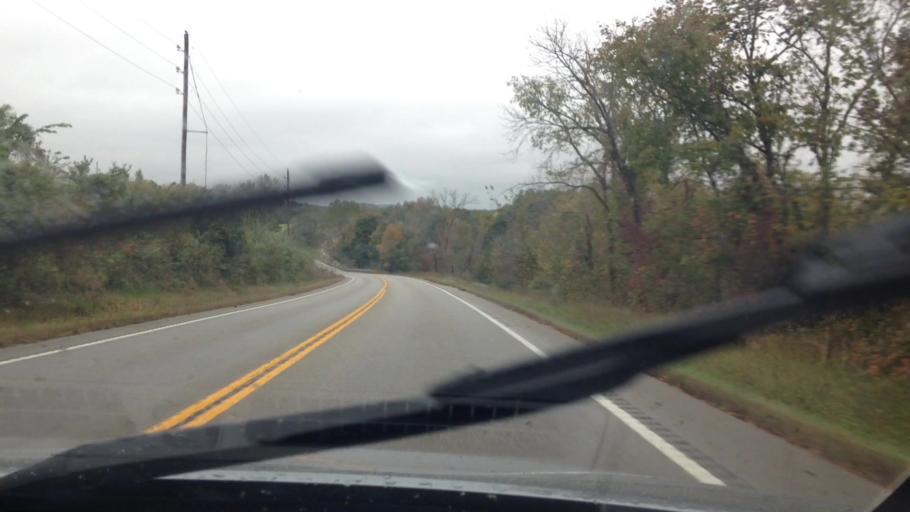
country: US
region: Missouri
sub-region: Platte County
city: Weston
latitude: 39.4083
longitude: -94.8692
